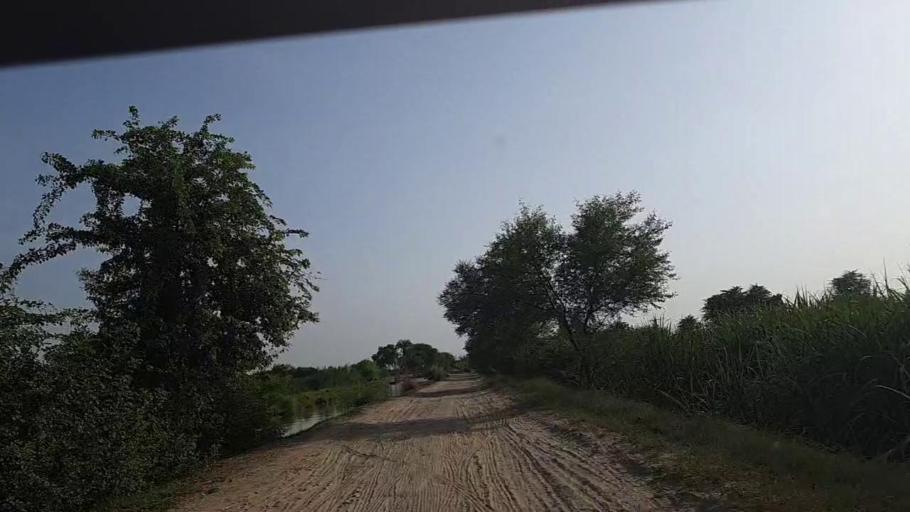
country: PK
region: Sindh
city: Ghotki
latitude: 27.9955
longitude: 69.2606
